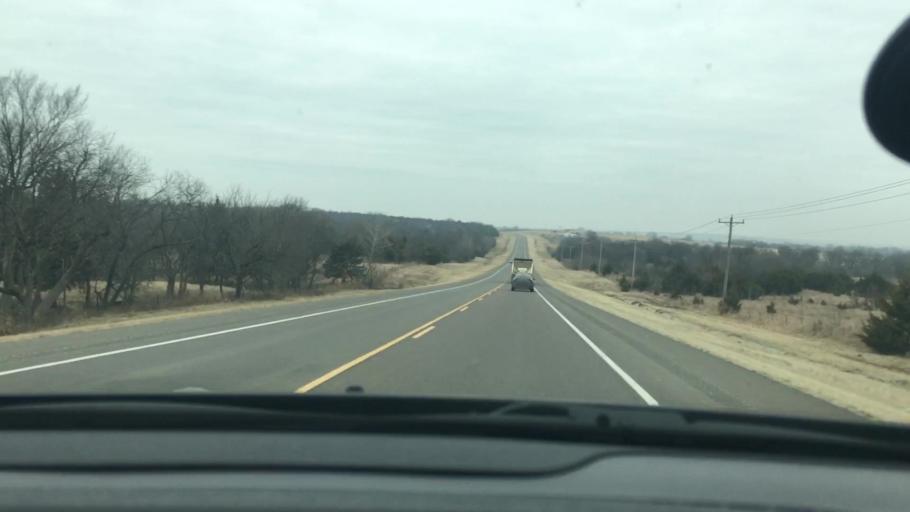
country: US
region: Oklahoma
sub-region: Murray County
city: Davis
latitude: 34.5132
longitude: -97.2005
